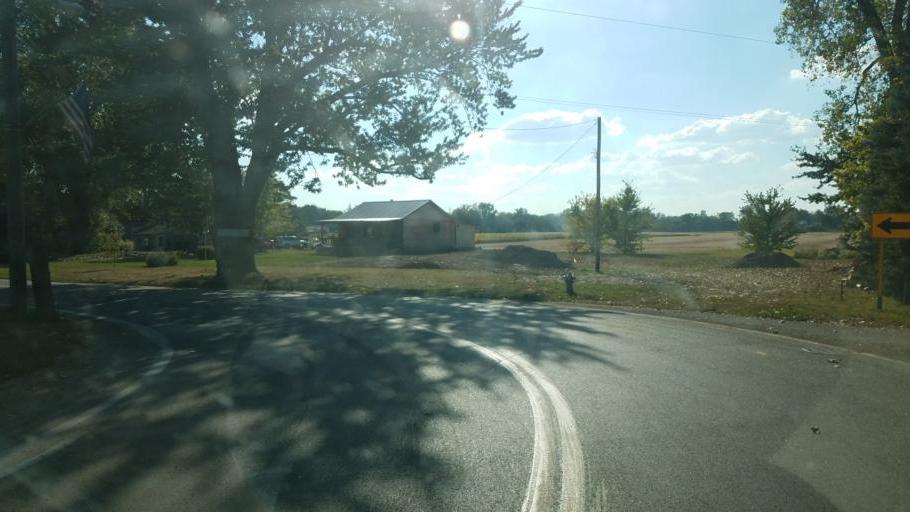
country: US
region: Ohio
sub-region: Union County
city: Richwood
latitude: 40.5857
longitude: -83.3844
